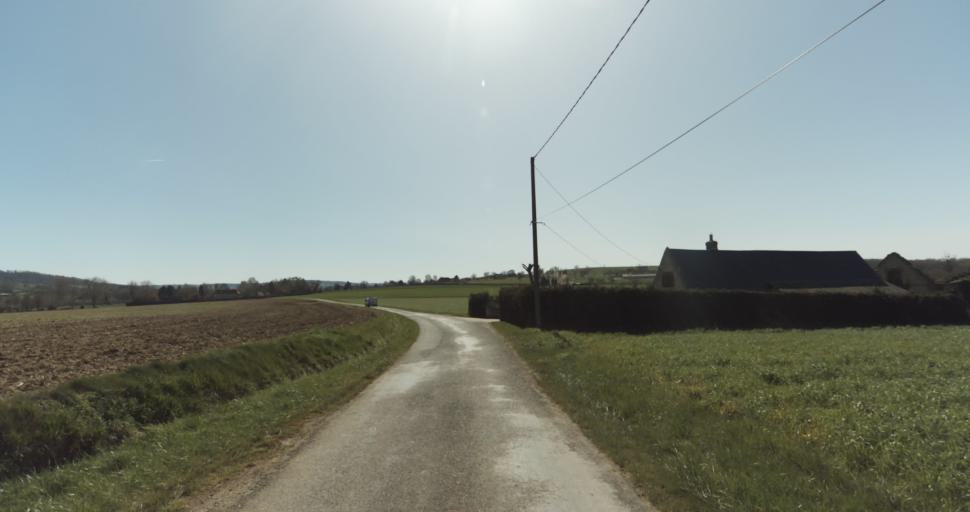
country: FR
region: Lower Normandy
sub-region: Departement du Calvados
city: Saint-Pierre-sur-Dives
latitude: 48.9967
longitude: 0.0238
